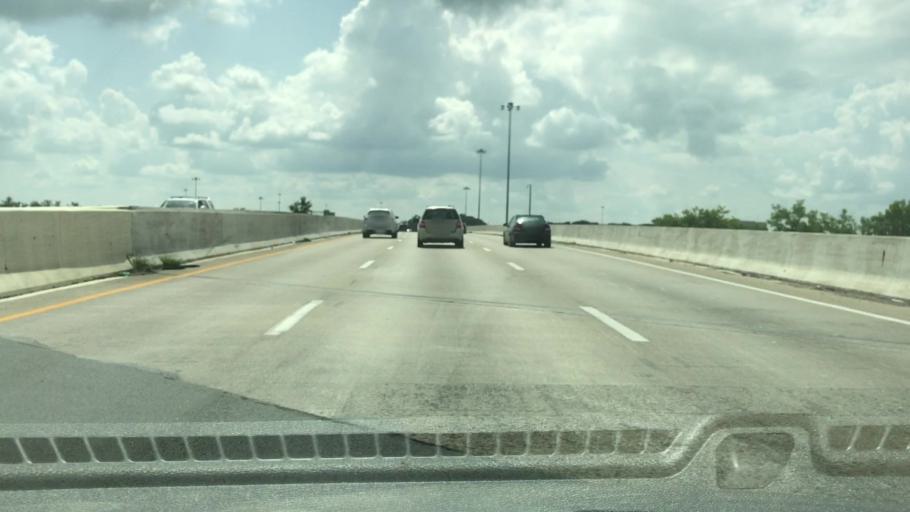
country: US
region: Ohio
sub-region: Franklin County
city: Grandview Heights
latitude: 39.9694
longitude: -83.0203
